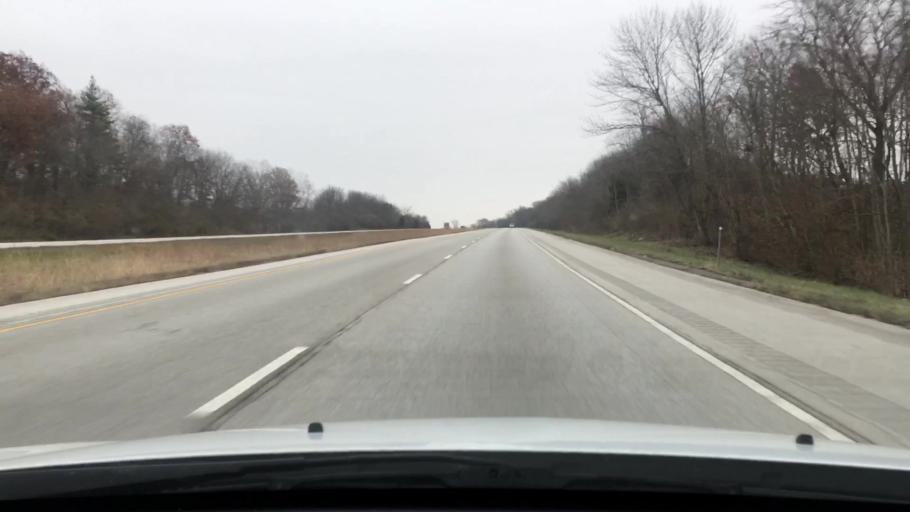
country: US
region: Illinois
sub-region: Scott County
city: Winchester
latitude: 39.6810
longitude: -90.3934
